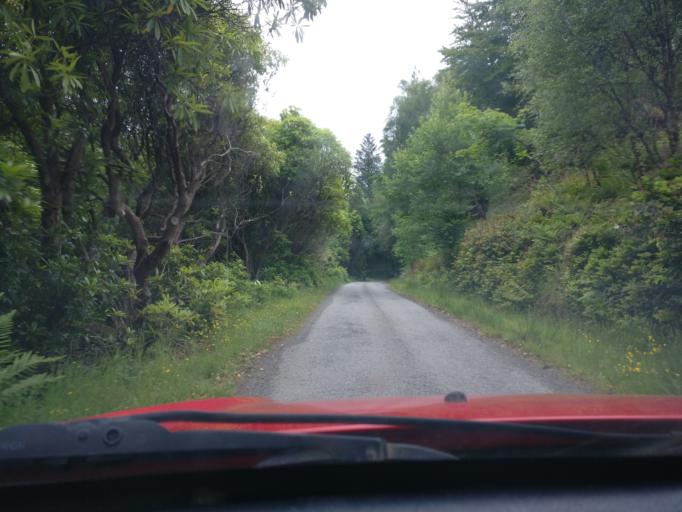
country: GB
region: Scotland
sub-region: Argyll and Bute
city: Isle Of Mull
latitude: 56.6093
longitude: -6.0482
